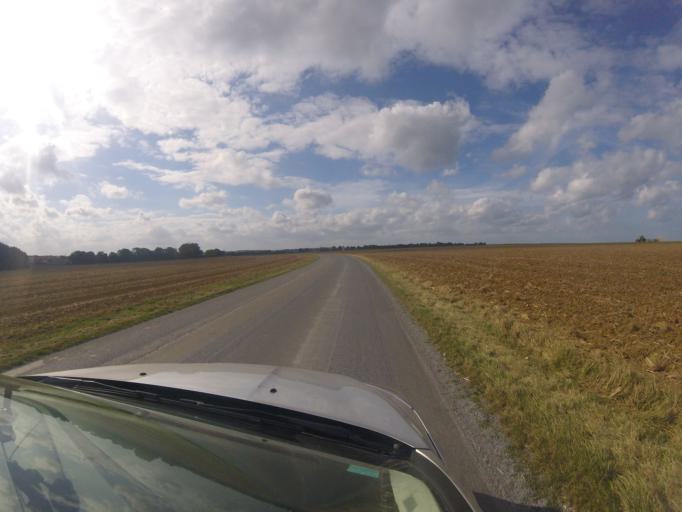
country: FR
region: Lower Normandy
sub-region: Departement du Calvados
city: Saint-Vigor-le-Grand
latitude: 49.3322
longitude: -0.6750
